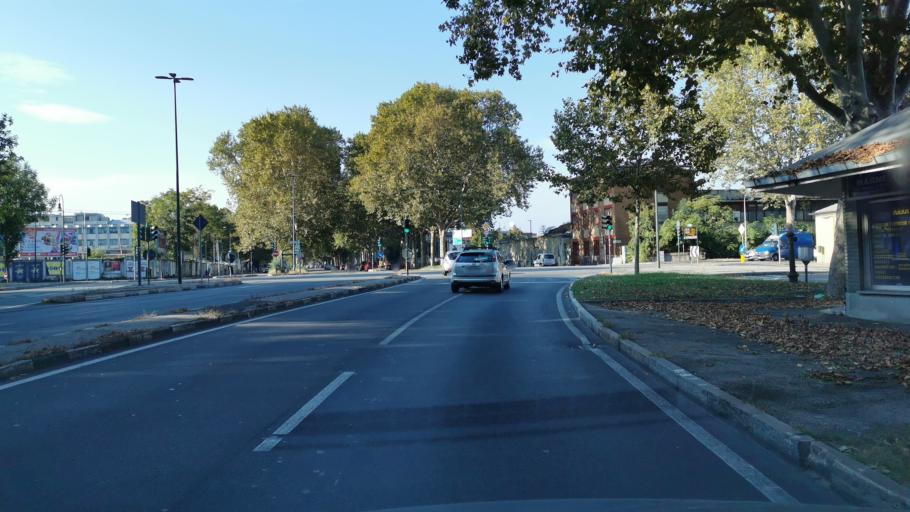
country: IT
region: Piedmont
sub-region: Provincia di Torino
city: Turin
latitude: 45.0792
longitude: 7.7010
